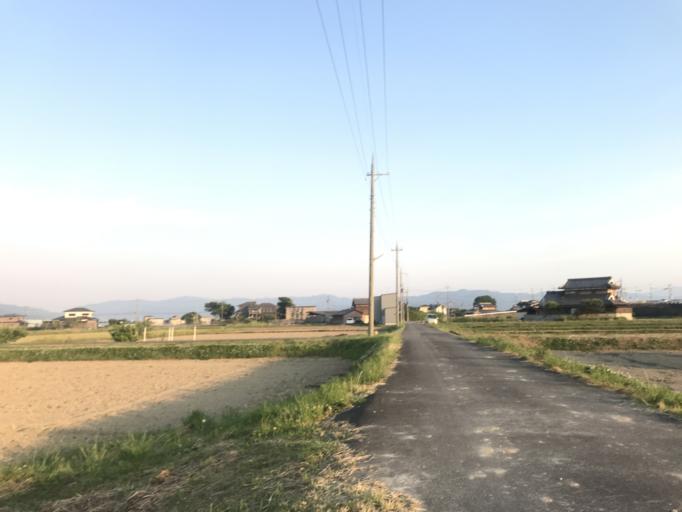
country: JP
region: Kyoto
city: Kameoka
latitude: 35.0541
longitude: 135.5527
